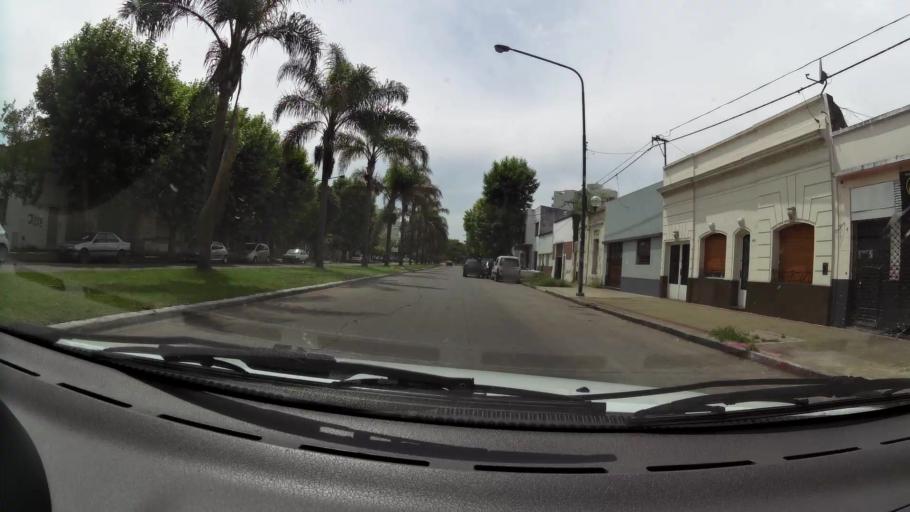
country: AR
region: Buenos Aires
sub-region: Partido de La Plata
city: La Plata
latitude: -34.9460
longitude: -57.9530
